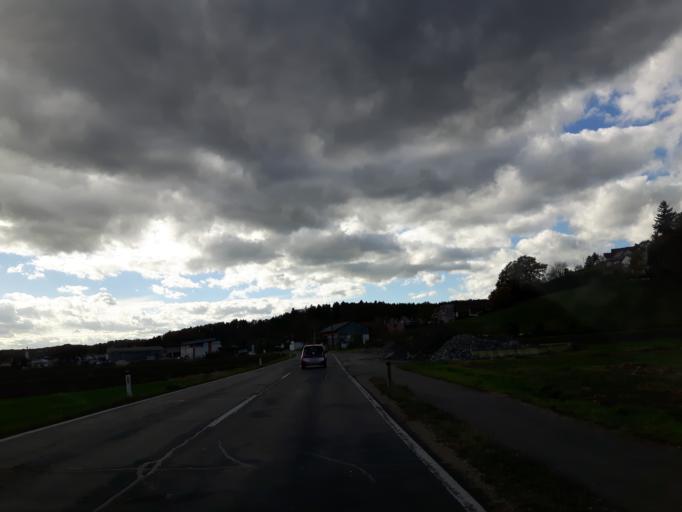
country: AT
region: Styria
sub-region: Politischer Bezirk Suedoststeiermark
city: Sankt Stefan im Rosental
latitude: 46.9174
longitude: 15.7143
